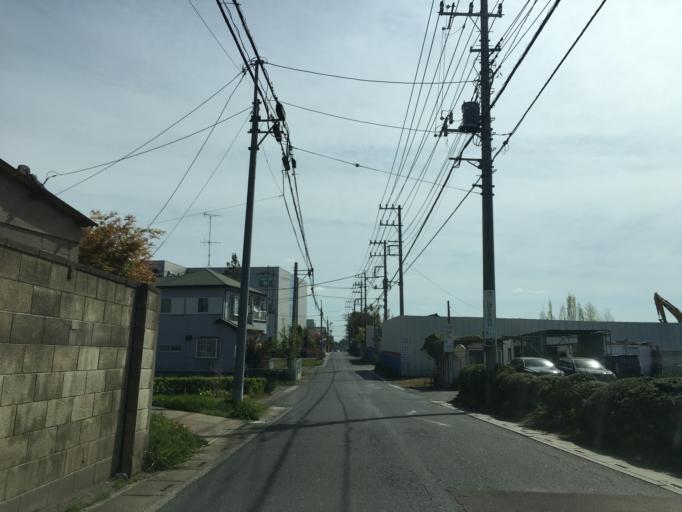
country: JP
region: Saitama
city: Hasuda
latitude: 35.9762
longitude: 139.6354
